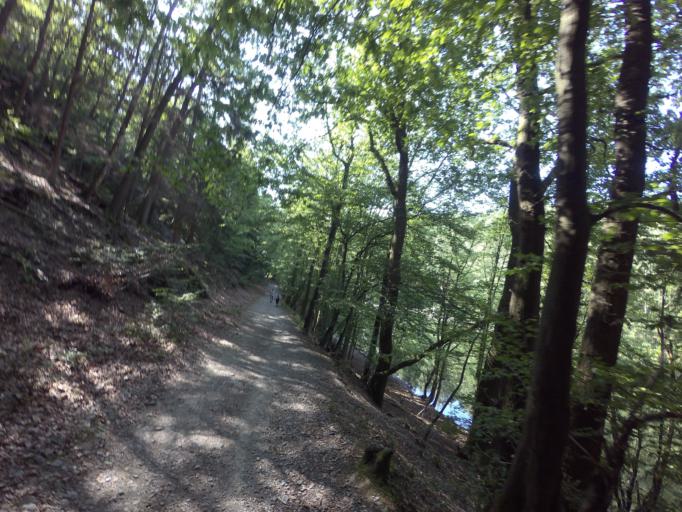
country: DE
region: North Rhine-Westphalia
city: Heimbach
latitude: 50.6044
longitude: 6.4004
